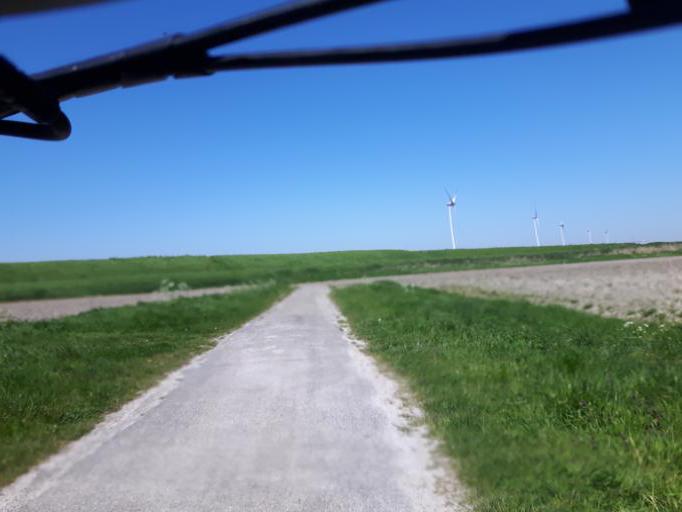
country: NL
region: Zeeland
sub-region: Gemeente Reimerswaal
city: Yerseke
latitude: 51.5510
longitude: 4.0526
